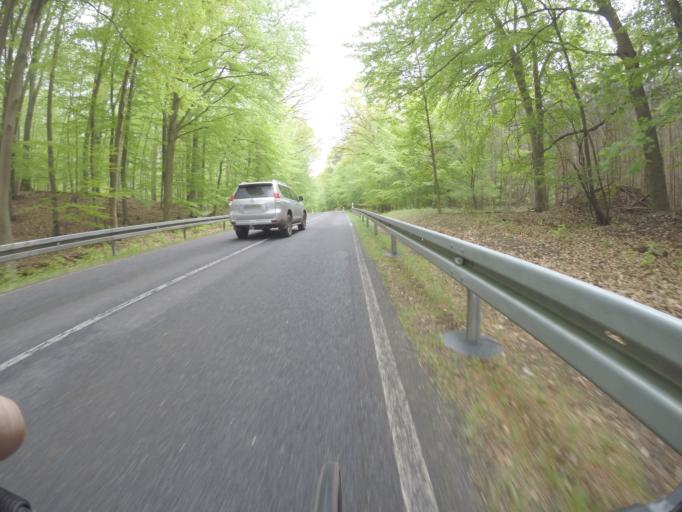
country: DE
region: Brandenburg
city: Joachimsthal
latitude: 52.9444
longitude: 13.7467
